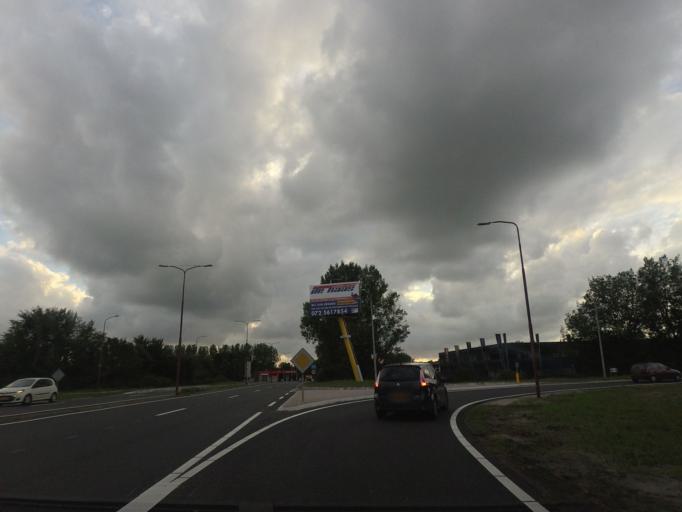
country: NL
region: North Holland
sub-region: Gemeente Alkmaar
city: Alkmaar
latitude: 52.6464
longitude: 4.7414
